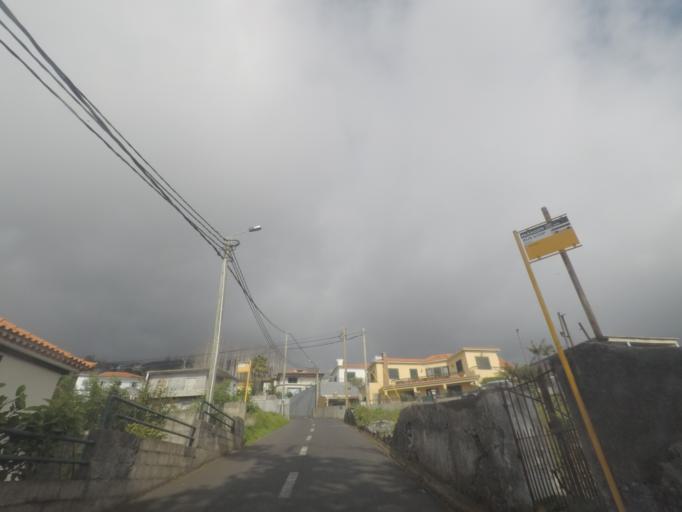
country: PT
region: Madeira
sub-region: Funchal
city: Nossa Senhora do Monte
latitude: 32.6709
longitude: -16.8991
